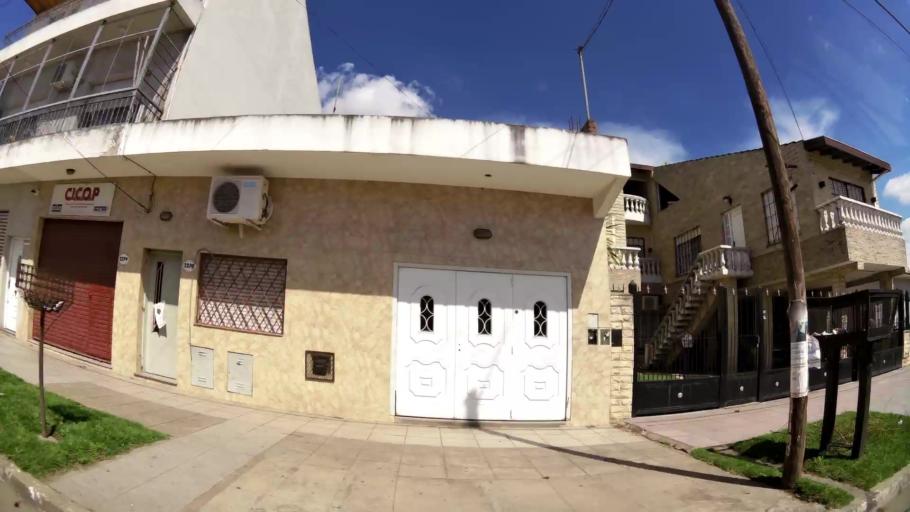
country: AR
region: Buenos Aires
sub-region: Partido de Quilmes
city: Quilmes
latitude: -34.8199
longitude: -58.2734
